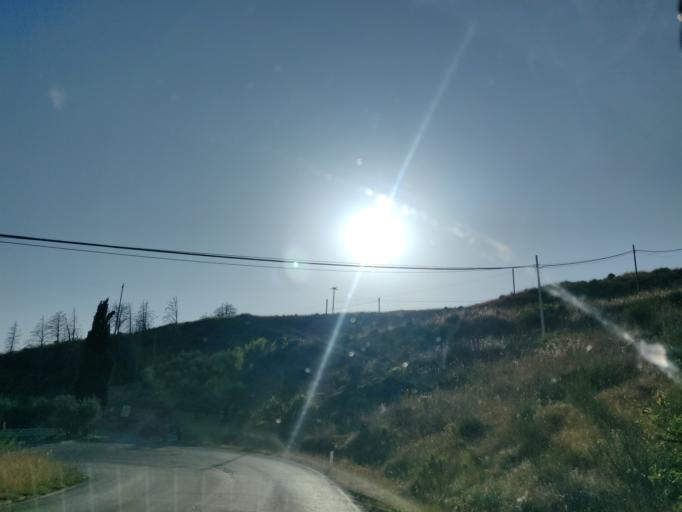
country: IT
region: Tuscany
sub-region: Provincia di Siena
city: Piancastagnaio
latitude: 42.8409
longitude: 11.7003
